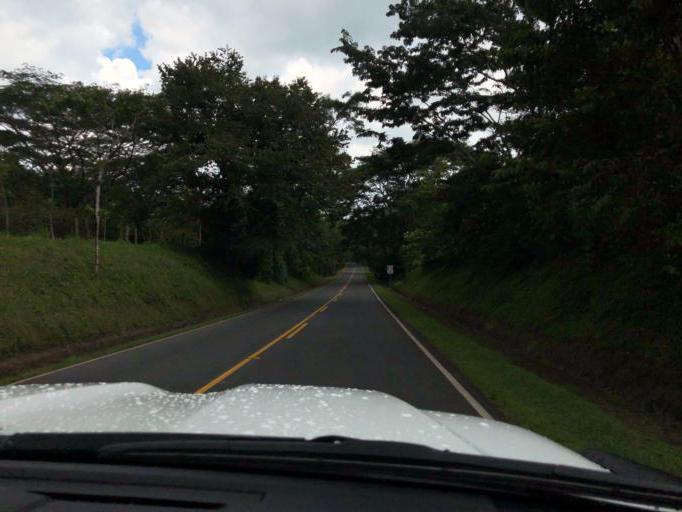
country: NI
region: Chontales
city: Villa Sandino
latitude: 11.9982
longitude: -84.8872
